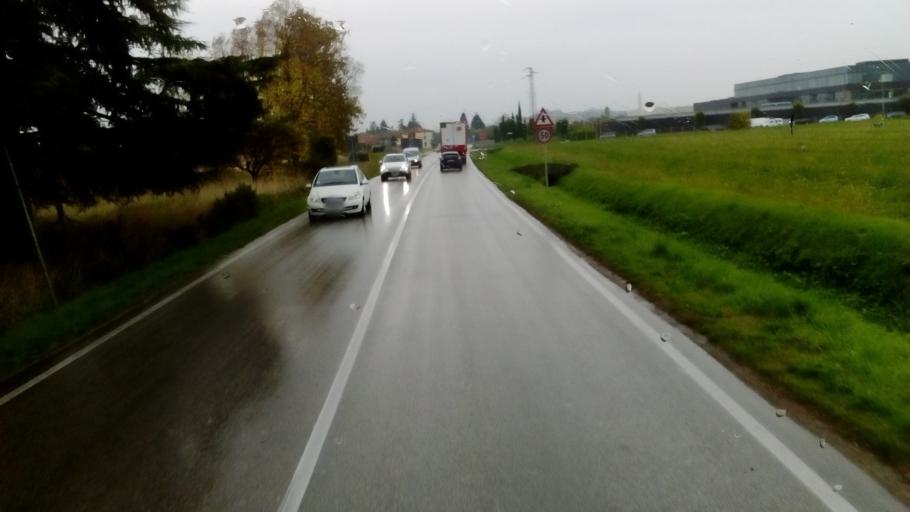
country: IT
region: Veneto
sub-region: Provincia di Vicenza
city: Breganze
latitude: 45.6951
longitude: 11.5633
